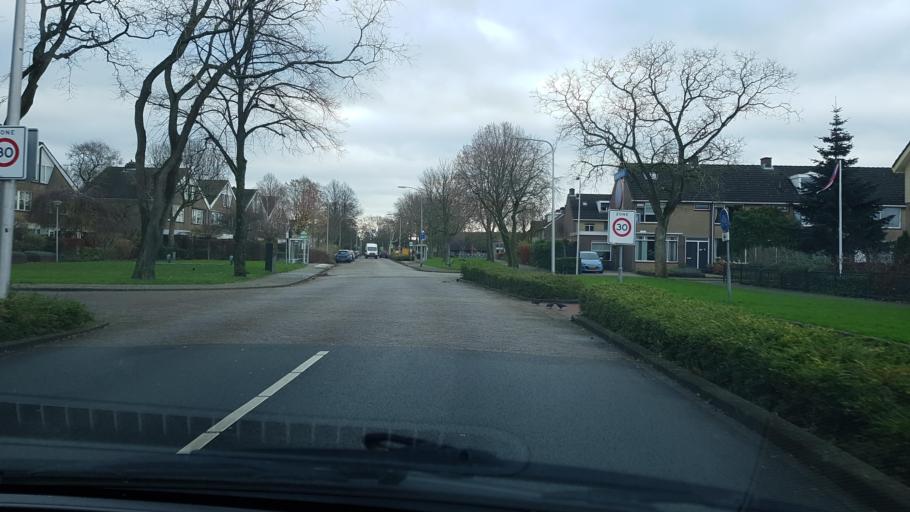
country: NL
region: South Holland
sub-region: Bodegraven-Reeuwijk
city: Bodegraven
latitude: 52.0788
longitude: 4.7481
